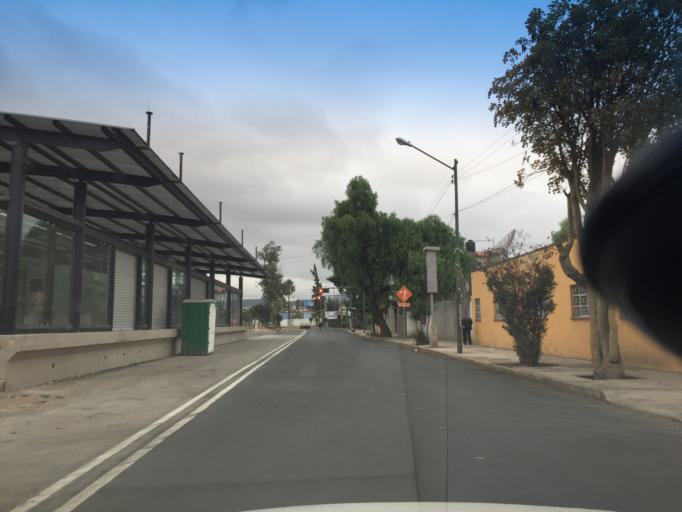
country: MX
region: Mexico City
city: Venustiano Carranza
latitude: 19.4696
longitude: -99.0646
